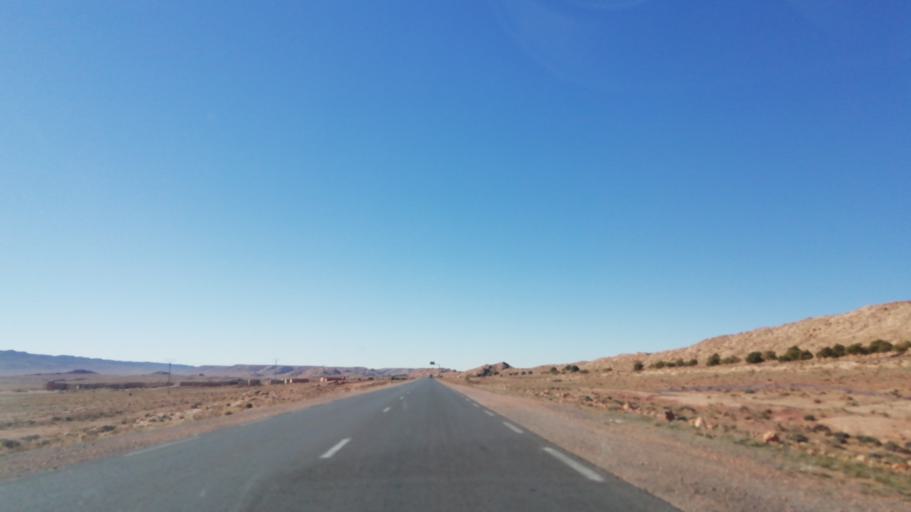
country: DZ
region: El Bayadh
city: El Bayadh
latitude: 33.6144
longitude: 1.1779
